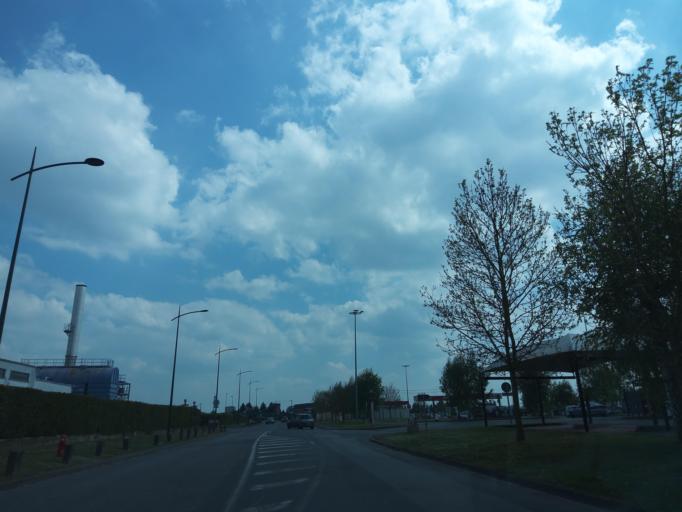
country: FR
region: Picardie
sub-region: Departement de l'Aisne
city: Laon
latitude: 49.5834
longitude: 3.6433
